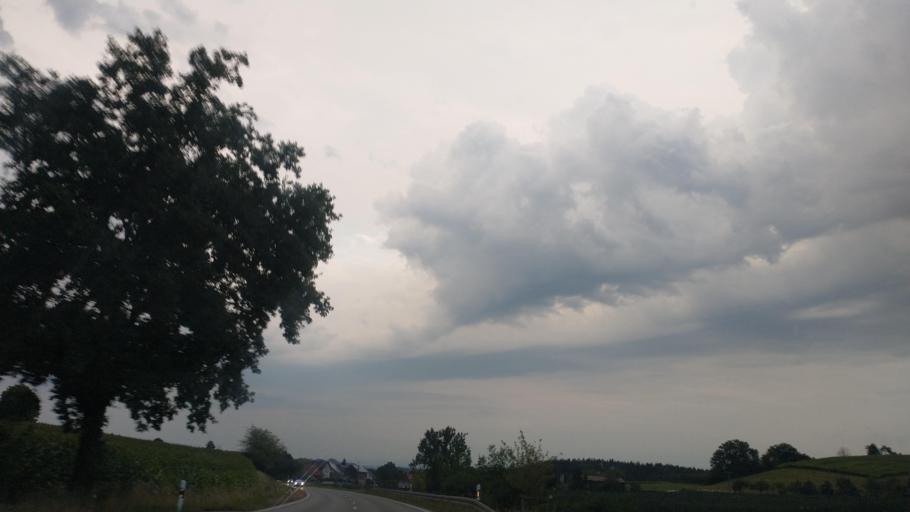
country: DE
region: Baden-Wuerttemberg
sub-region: Tuebingen Region
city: Tettnang
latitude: 47.6646
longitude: 9.6230
